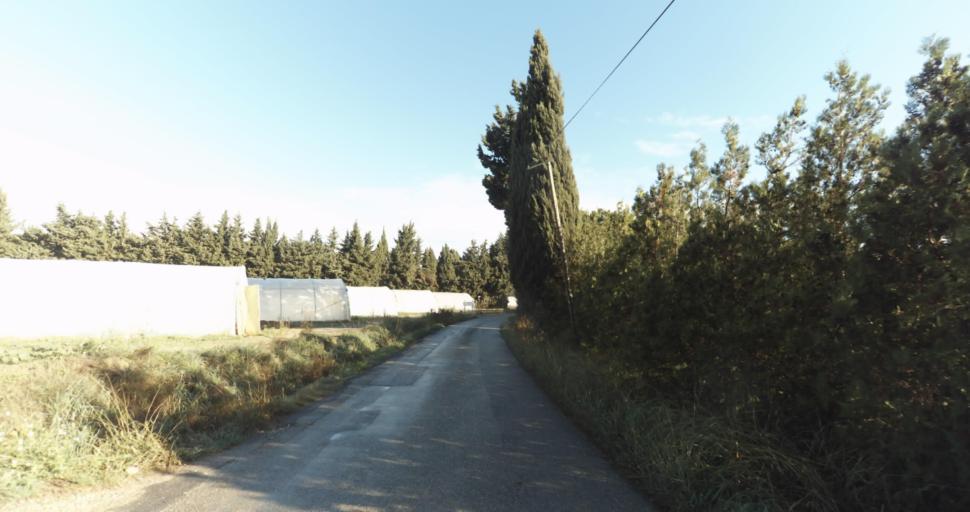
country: FR
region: Provence-Alpes-Cote d'Azur
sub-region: Departement des Bouches-du-Rhone
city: Rognonas
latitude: 43.8894
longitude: 4.7951
